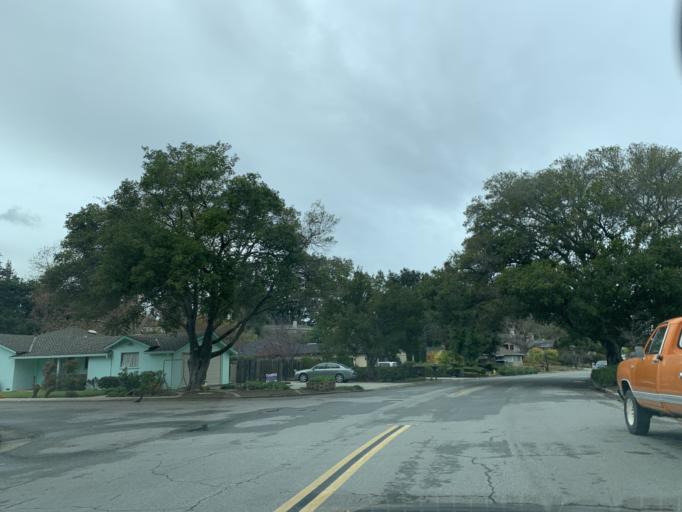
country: US
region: California
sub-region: Santa Clara County
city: Cupertino
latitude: 37.3310
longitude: -122.0624
